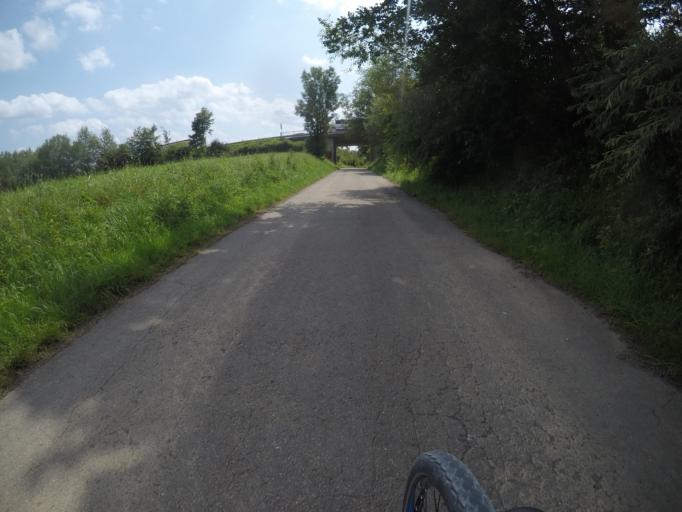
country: DE
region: Baden-Wuerttemberg
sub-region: Freiburg Region
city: Zimmern ob Rottweil
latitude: 48.1783
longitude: 8.6016
